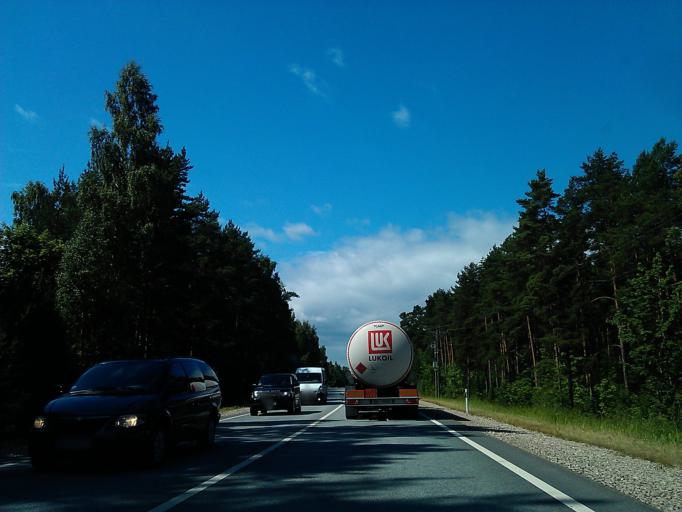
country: LV
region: Jurmala
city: Jurmala
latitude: 56.9309
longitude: 23.6960
